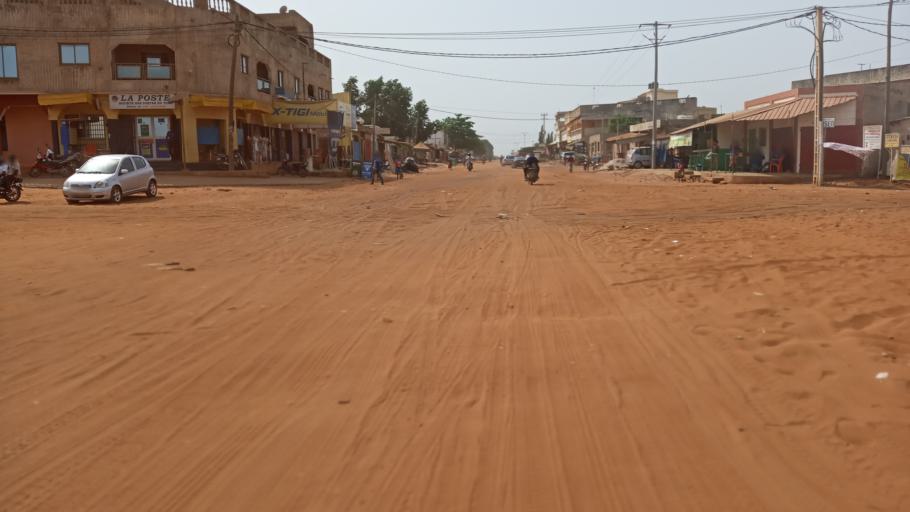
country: TG
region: Maritime
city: Lome
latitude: 6.2043
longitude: 1.1651
